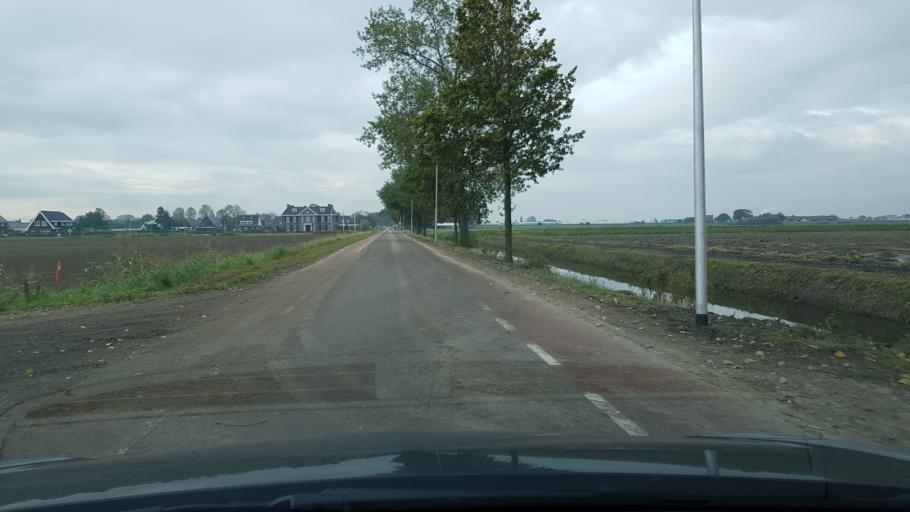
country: NL
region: North Holland
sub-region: Gemeente Aalsmeer
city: Aalsmeer
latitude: 52.2503
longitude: 4.7917
